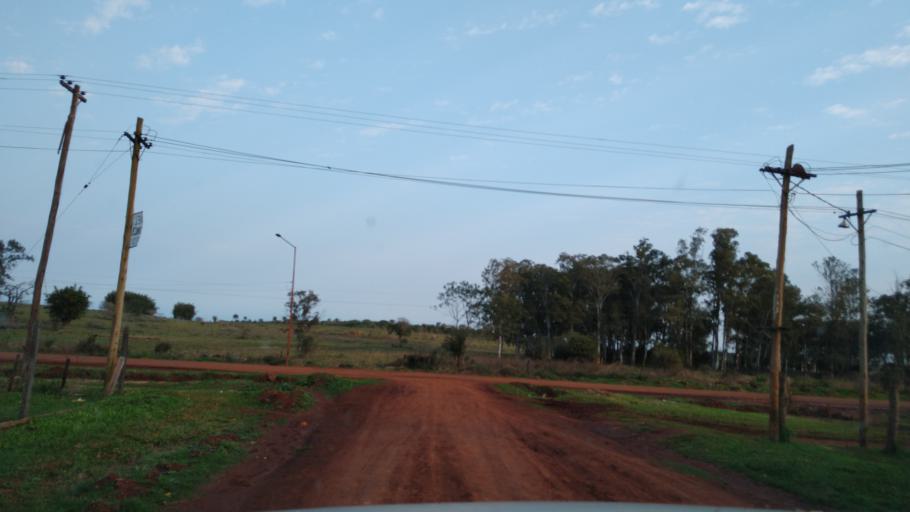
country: AR
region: Corrientes
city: San Carlos
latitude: -27.7517
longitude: -55.9005
